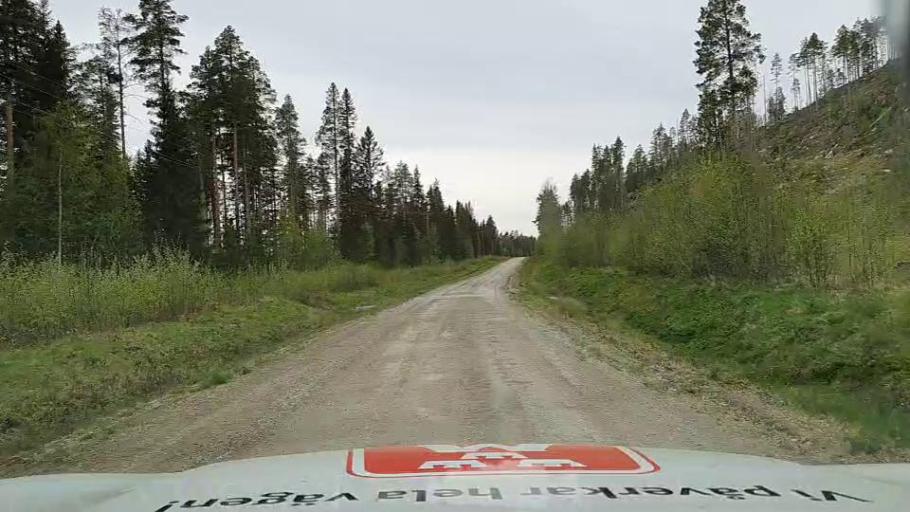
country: SE
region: Jaemtland
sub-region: Bergs Kommun
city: Hoverberg
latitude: 62.6713
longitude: 14.8058
